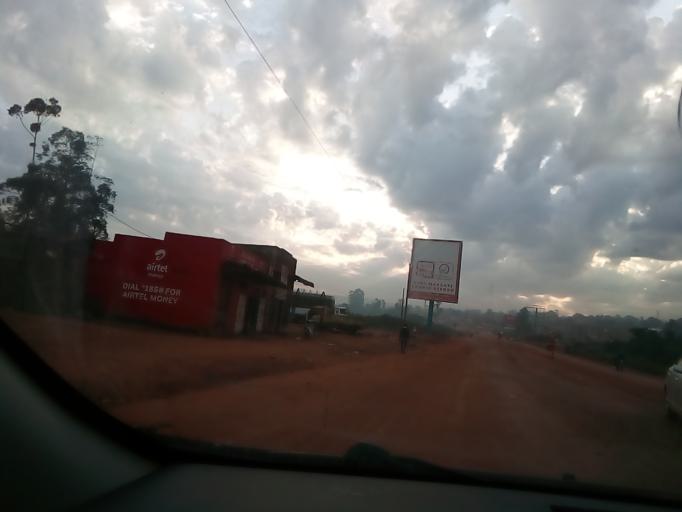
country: UG
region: Central Region
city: Masaka
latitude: -0.3290
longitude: 31.7477
